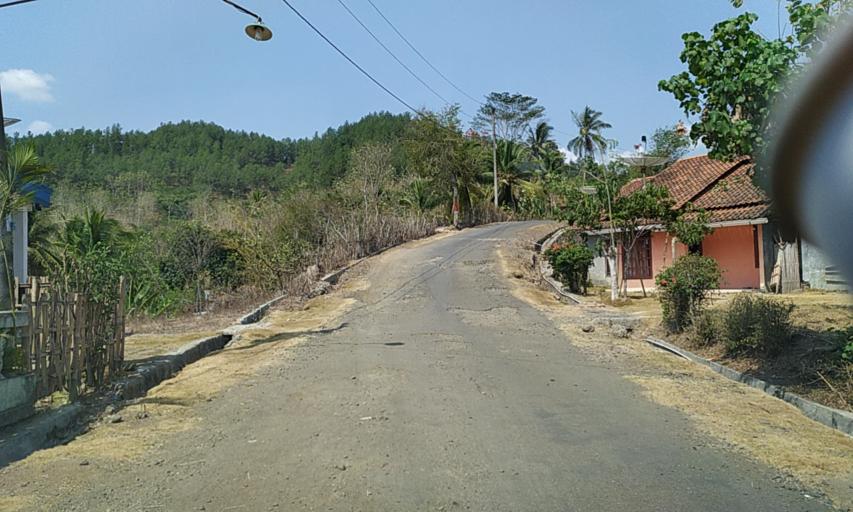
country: ID
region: Central Java
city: Cidadap
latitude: -7.3984
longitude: 108.8525
